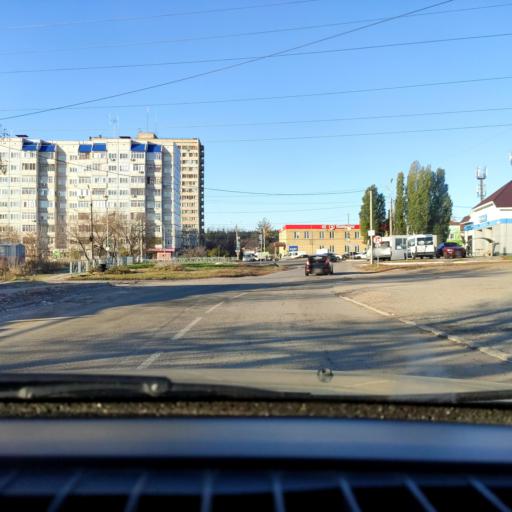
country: RU
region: Samara
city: Tol'yatti
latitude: 53.5338
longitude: 49.3971
